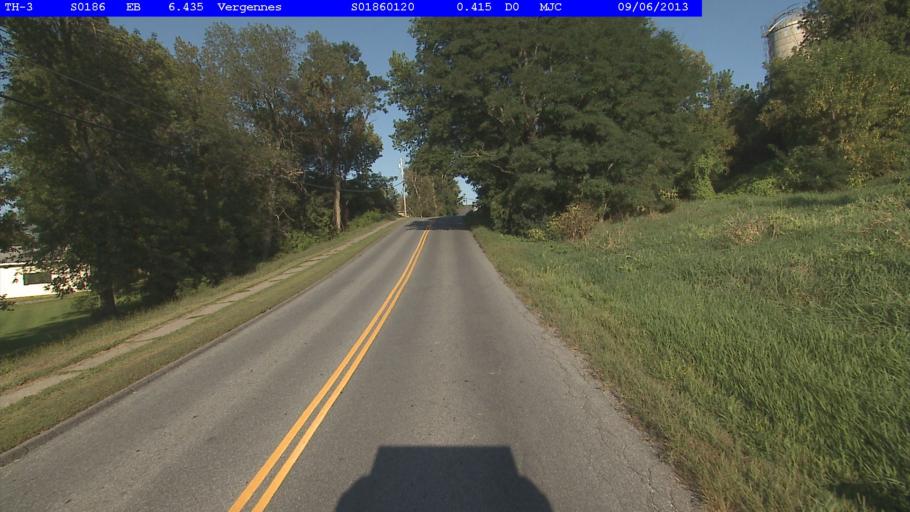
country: US
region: Vermont
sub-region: Addison County
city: Vergennes
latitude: 44.1632
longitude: -73.2618
